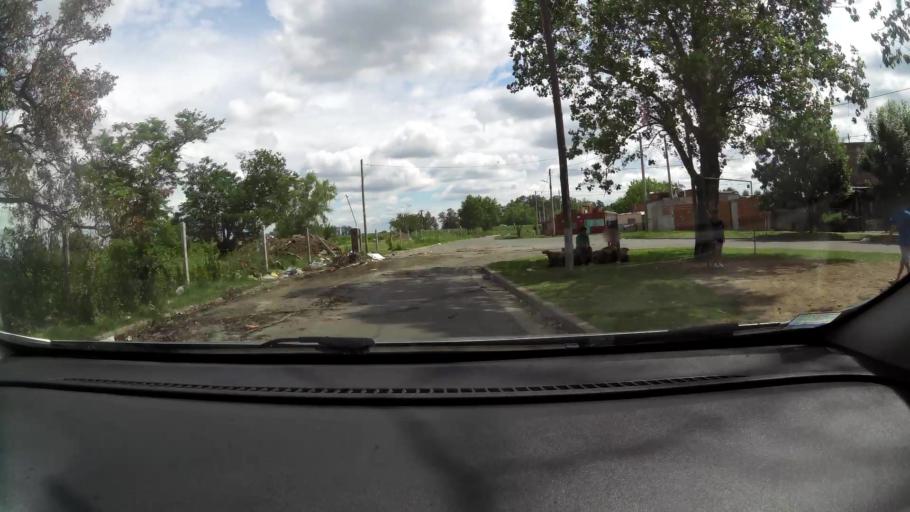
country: AR
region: Santa Fe
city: Gobernador Galvez
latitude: -33.0146
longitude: -60.6382
